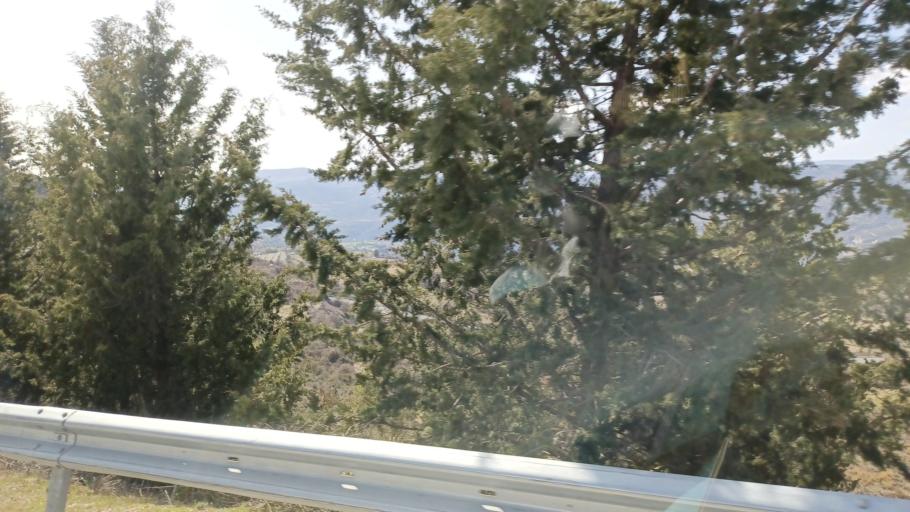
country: CY
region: Limassol
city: Pachna
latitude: 34.8607
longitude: 32.7632
